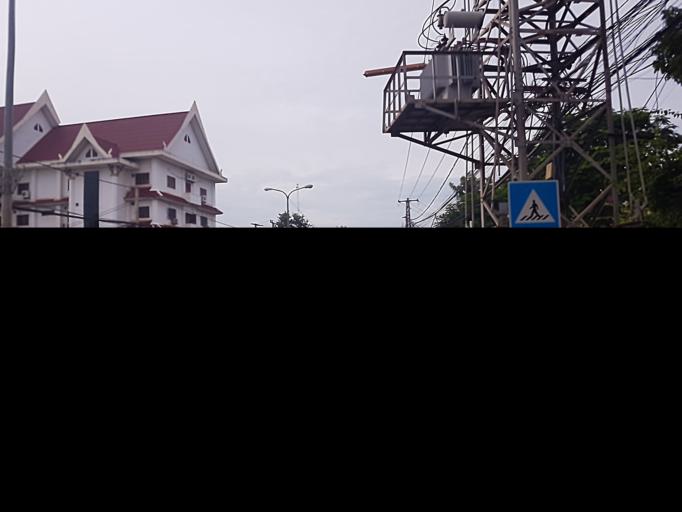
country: LA
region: Vientiane
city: Vientiane
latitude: 17.9466
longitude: 102.6200
